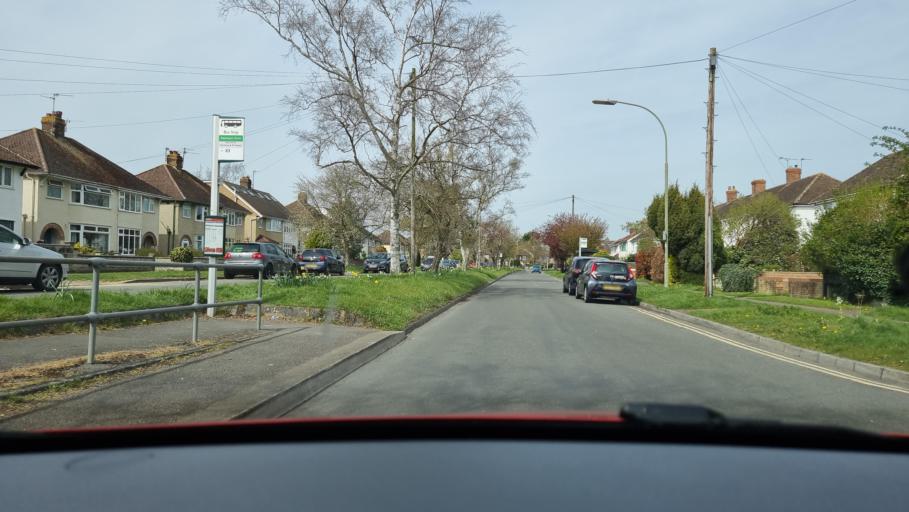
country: GB
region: England
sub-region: Oxfordshire
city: Oxford
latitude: 51.7675
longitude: -1.2367
